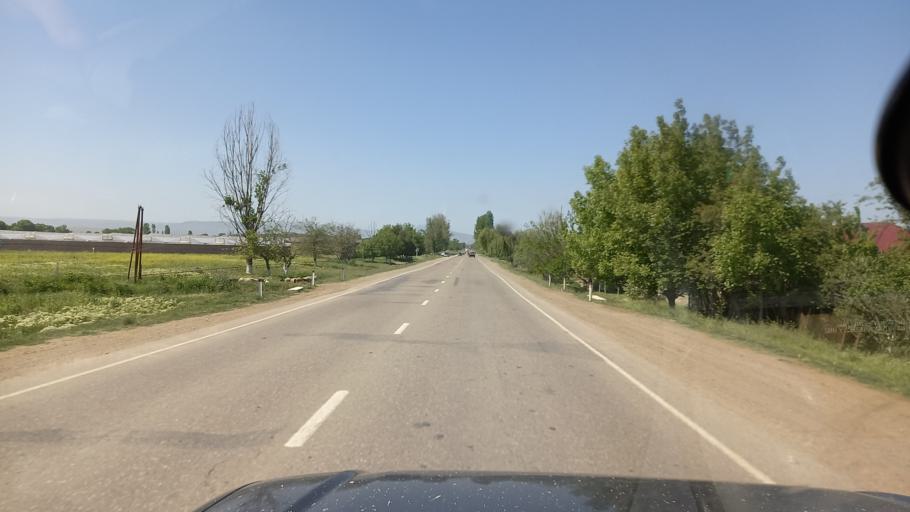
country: RU
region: Dagestan
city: Novaya Maka
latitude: 41.8294
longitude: 48.3869
